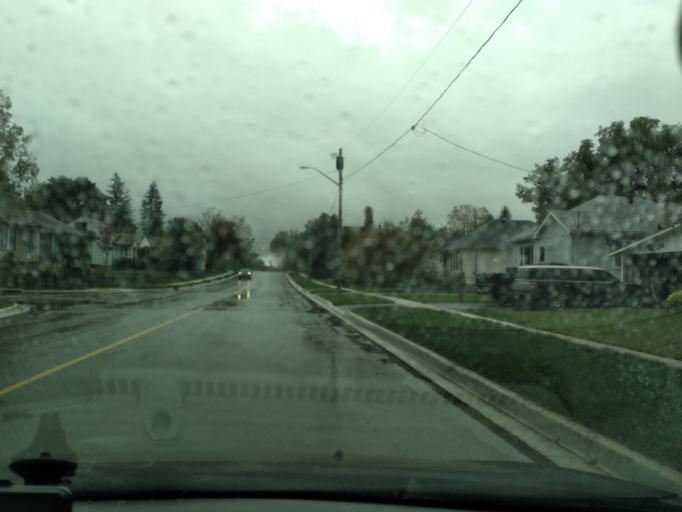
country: CA
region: Ontario
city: Barrie
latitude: 44.4008
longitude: -79.6755
